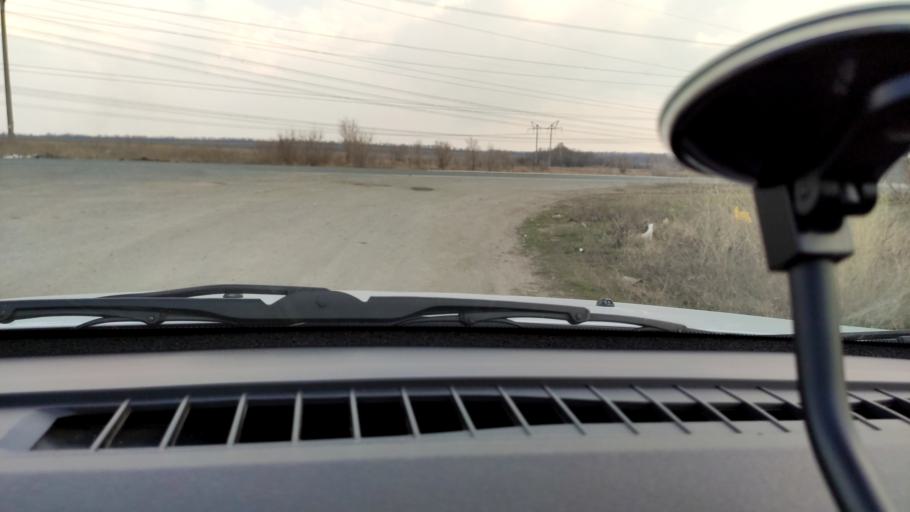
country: RU
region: Samara
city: Smyshlyayevka
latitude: 53.0906
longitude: 50.3965
